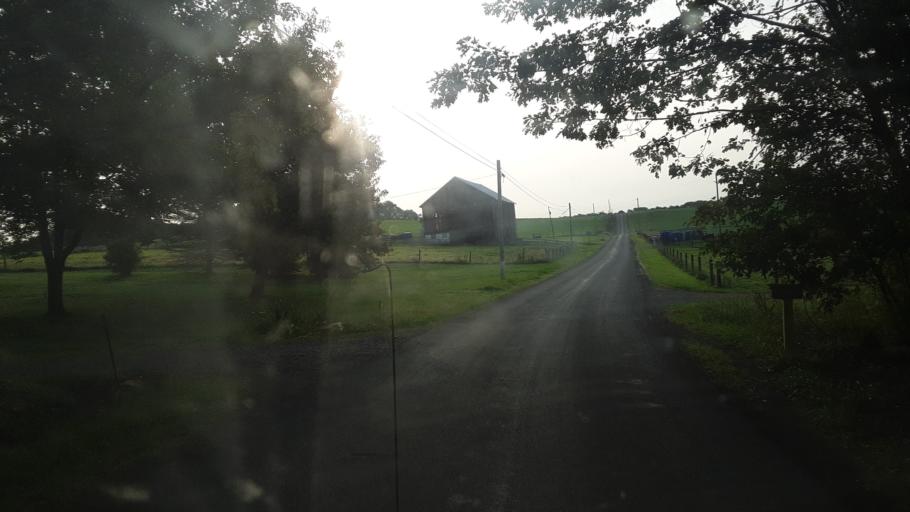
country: US
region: Pennsylvania
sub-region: Jefferson County
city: Punxsutawney
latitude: 40.9403
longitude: -79.2078
